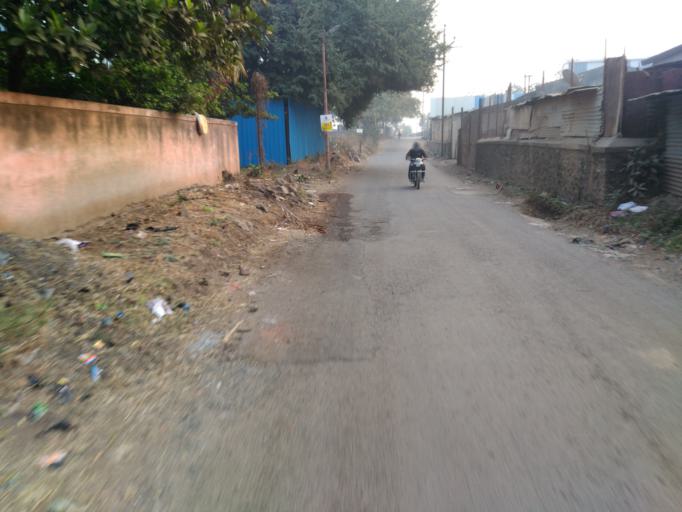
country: IN
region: Maharashtra
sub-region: Pune Division
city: Pune
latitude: 18.4586
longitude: 73.8956
